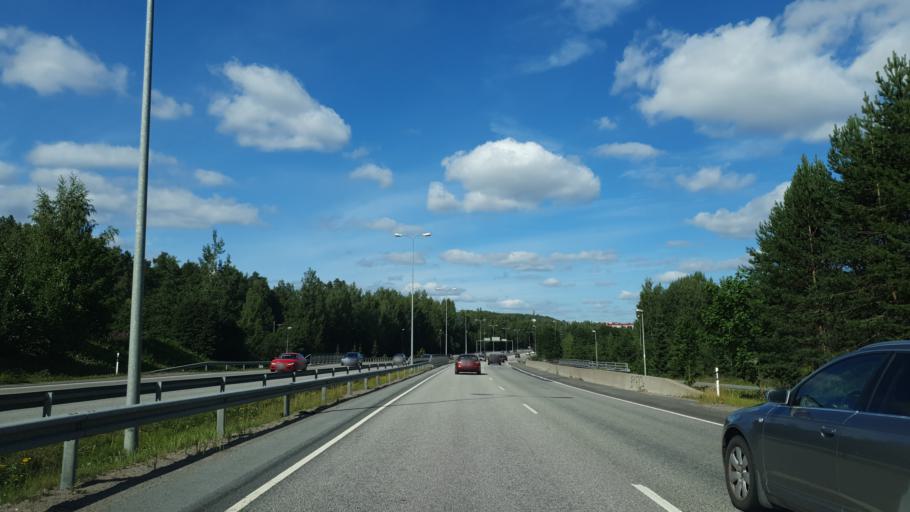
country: FI
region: Central Finland
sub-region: Jyvaeskylae
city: Jyvaeskylae
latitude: 62.2250
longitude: 25.7265
